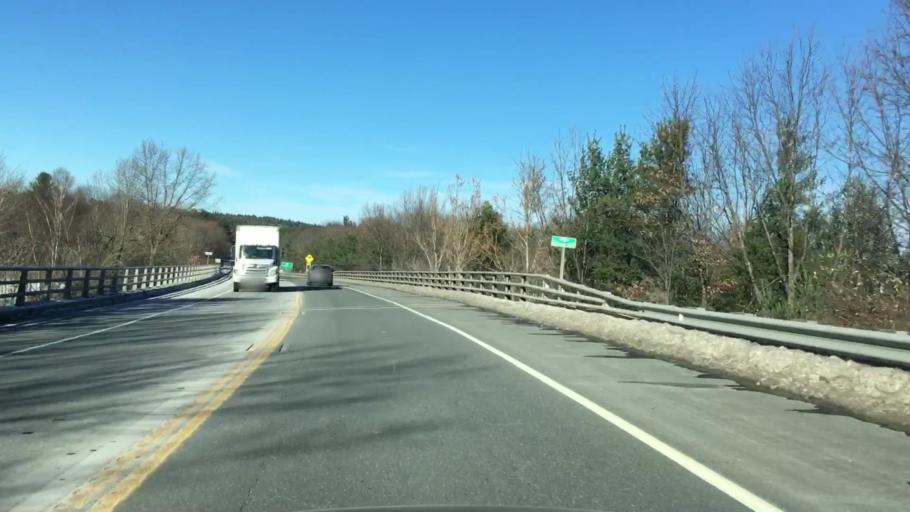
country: US
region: New Hampshire
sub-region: Hillsborough County
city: Milford
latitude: 42.8265
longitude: -71.6169
